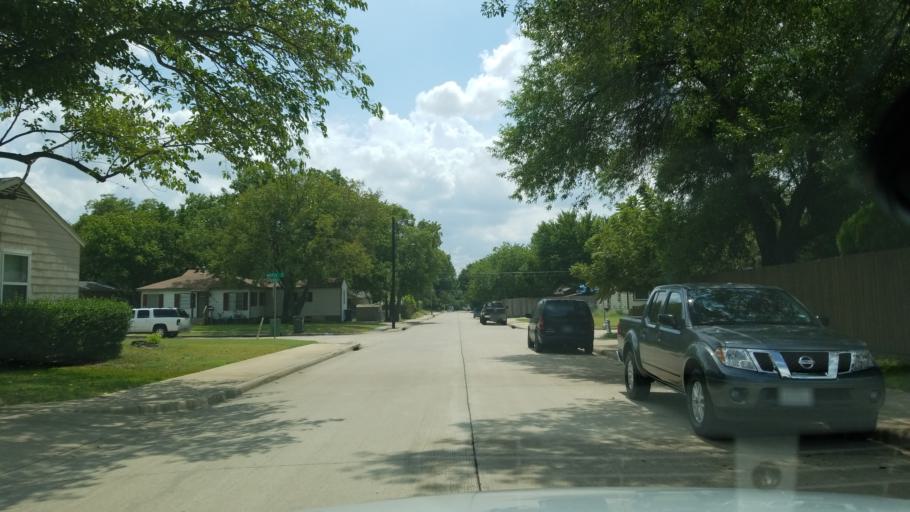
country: US
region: Texas
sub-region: Dallas County
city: Garland
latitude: 32.9193
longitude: -96.6520
